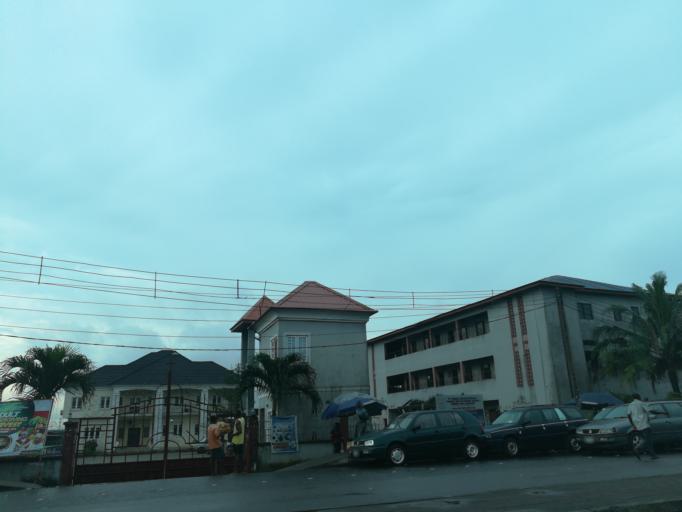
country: NG
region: Rivers
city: Port Harcourt
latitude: 4.7971
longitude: 6.9929
